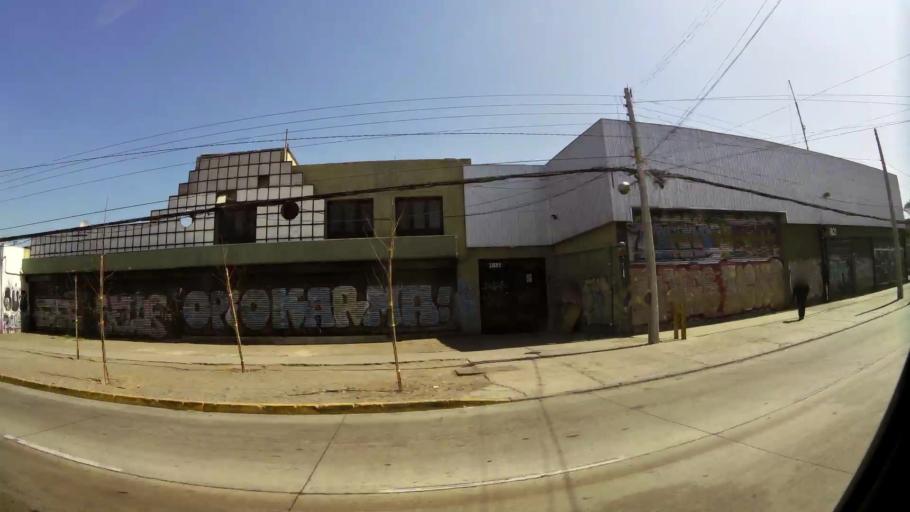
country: CL
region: Santiago Metropolitan
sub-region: Provincia de Santiago
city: Santiago
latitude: -33.4697
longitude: -70.6423
